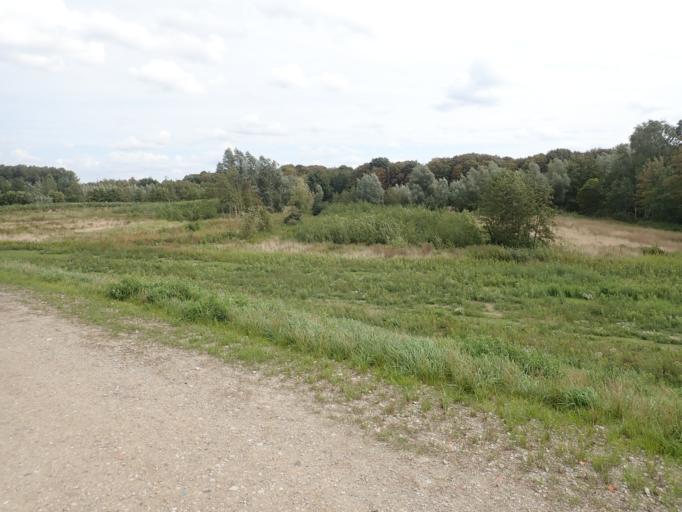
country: BE
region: Flanders
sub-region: Provincie Oost-Vlaanderen
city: Hamme
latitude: 51.0980
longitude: 4.1659
